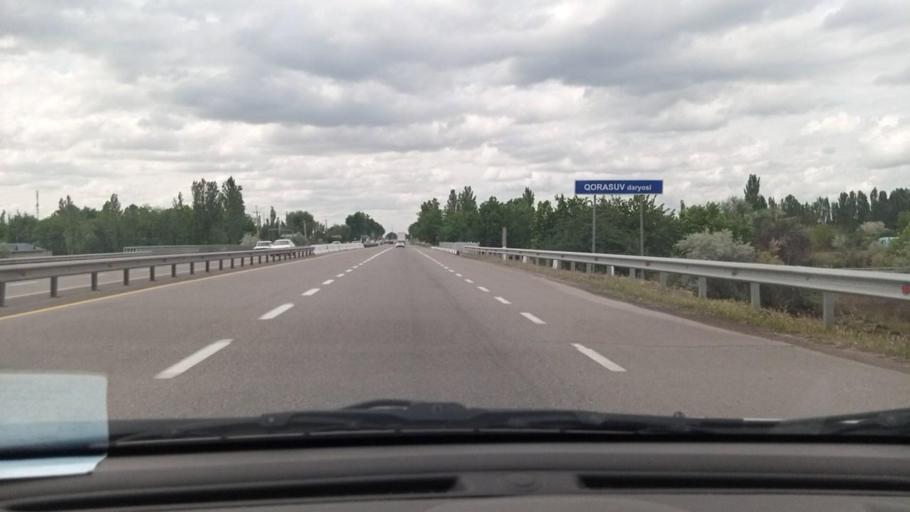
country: UZ
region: Toshkent Shahri
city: Bektemir
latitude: 41.1506
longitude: 69.4275
